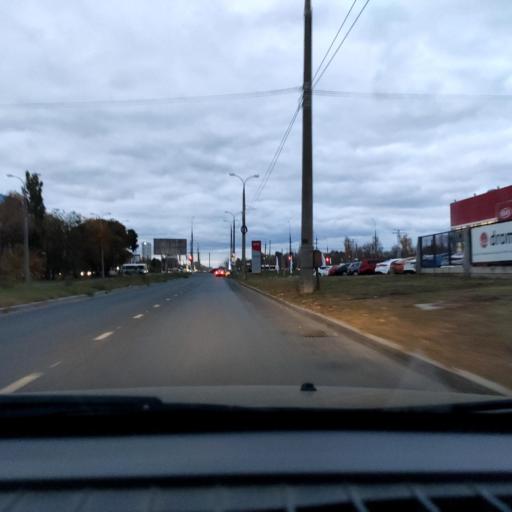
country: RU
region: Samara
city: Tol'yatti
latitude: 53.5537
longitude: 49.3033
